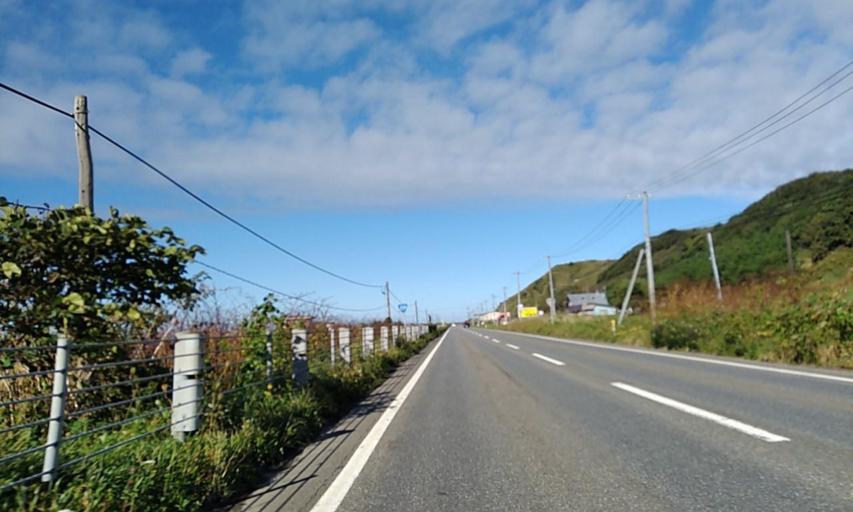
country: JP
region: Hokkaido
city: Shizunai-furukawacho
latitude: 42.3105
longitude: 142.4120
